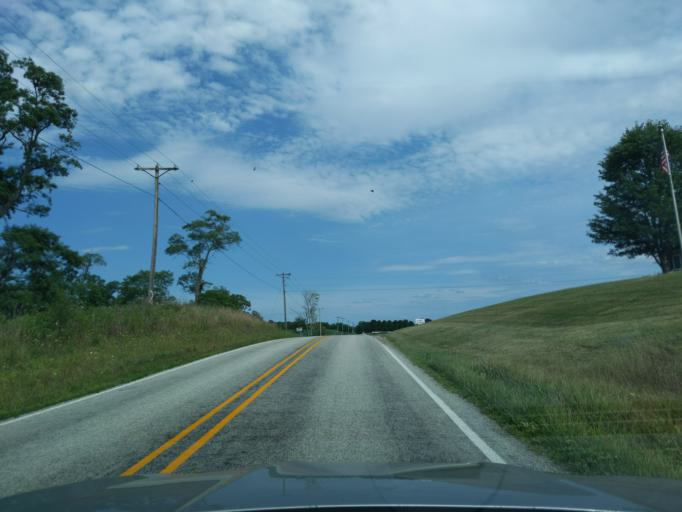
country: US
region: Indiana
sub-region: Ripley County
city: Osgood
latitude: 39.1950
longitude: -85.2322
